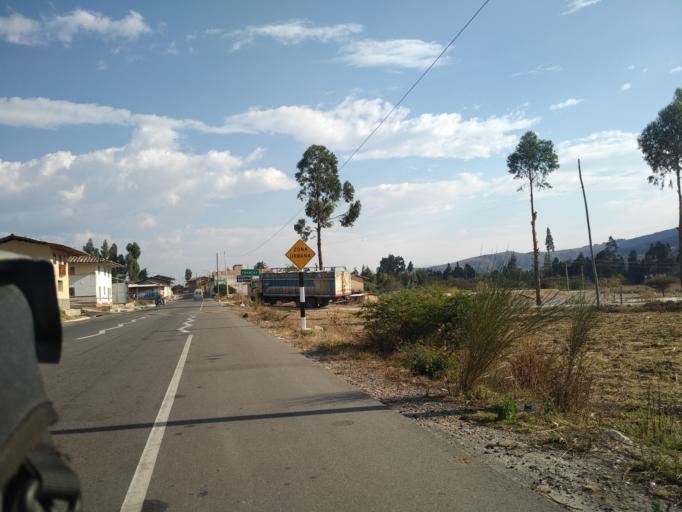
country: PE
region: Cajamarca
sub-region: San Marcos
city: San Marcos
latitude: -7.3826
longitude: -78.1255
